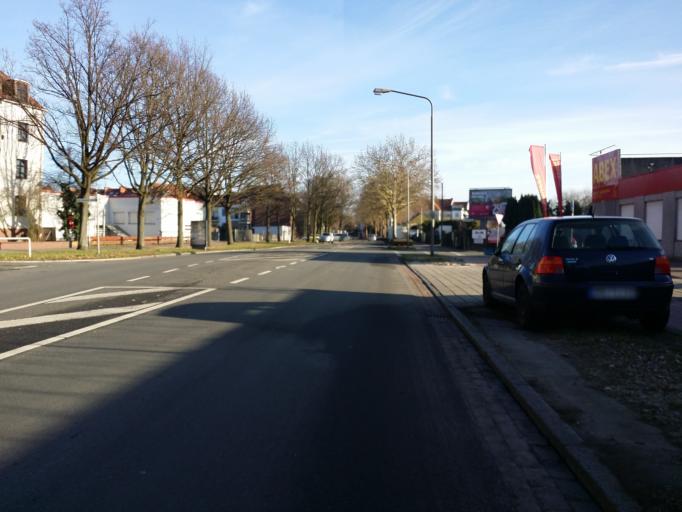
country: DE
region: Bremen
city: Bremen
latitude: 53.0760
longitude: 8.7797
